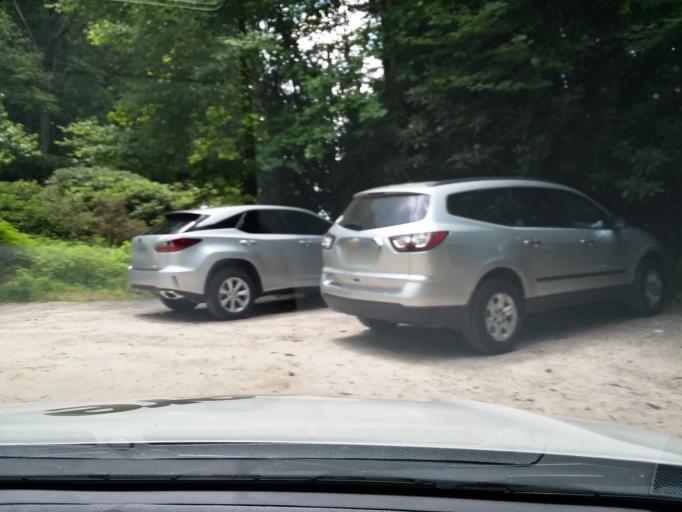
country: US
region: Georgia
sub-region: Rabun County
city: Mountain City
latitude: 35.0333
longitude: -83.2357
